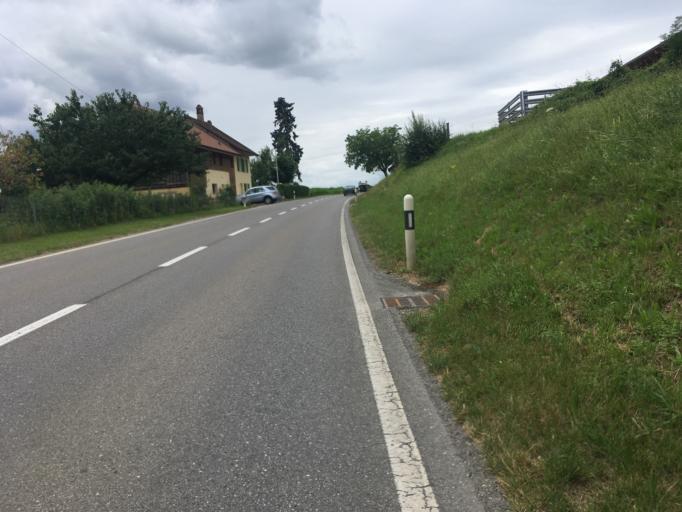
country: CH
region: Fribourg
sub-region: Broye District
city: Domdidier
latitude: 46.8849
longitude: 6.9779
